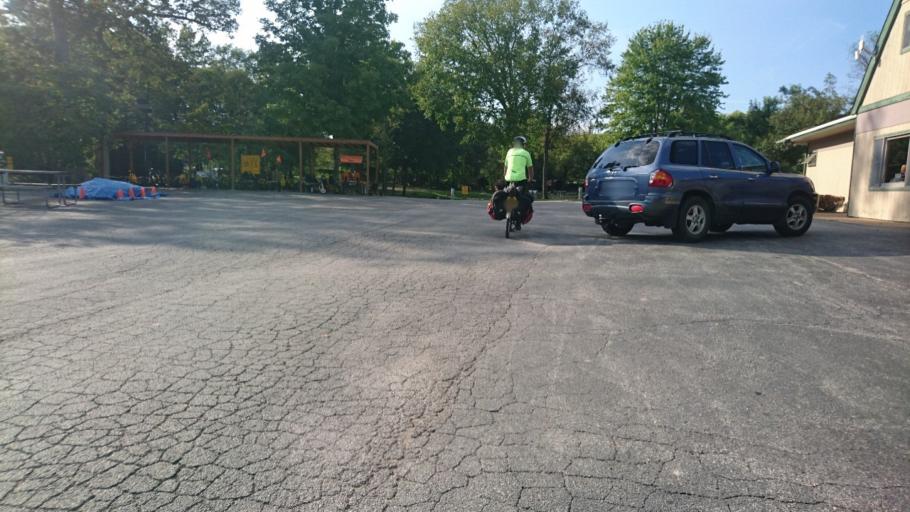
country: US
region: Missouri
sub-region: Franklin County
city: Pacific
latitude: 38.5008
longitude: -90.6890
